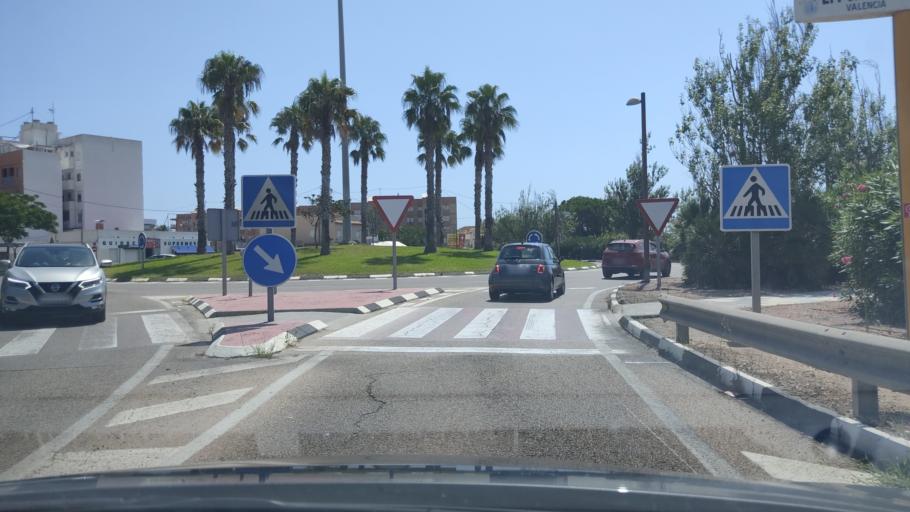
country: ES
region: Valencia
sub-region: Provincia de Valencia
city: Sollana
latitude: 39.3075
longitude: -0.2982
